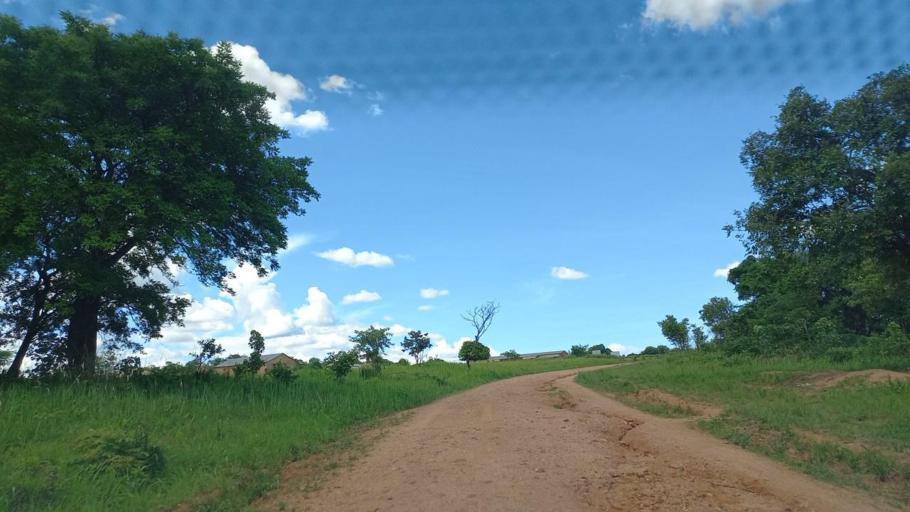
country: ZM
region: North-Western
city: Mwinilunga
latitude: -12.2461
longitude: 24.2759
